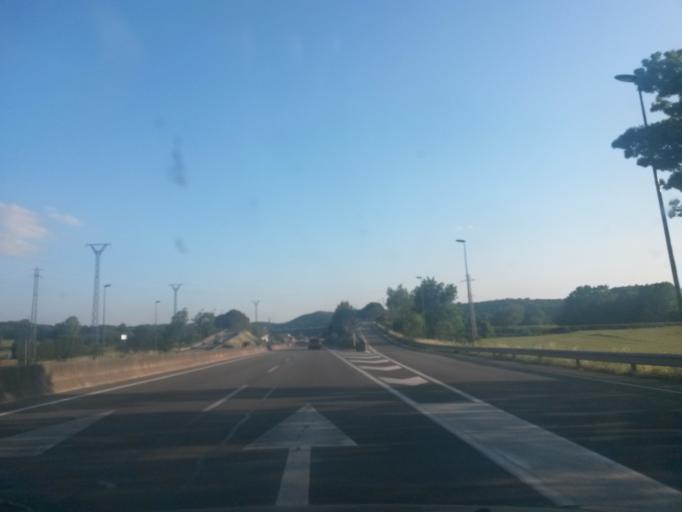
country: ES
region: Catalonia
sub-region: Provincia de Girona
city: Cornella del Terri
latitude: 42.0751
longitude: 2.8163
